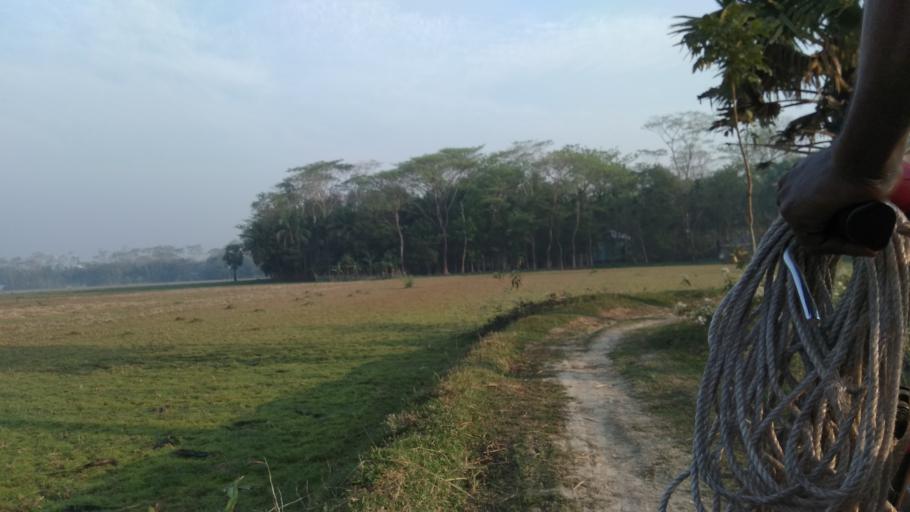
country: BD
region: Barisal
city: Mehendiganj
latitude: 22.9357
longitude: 90.4136
